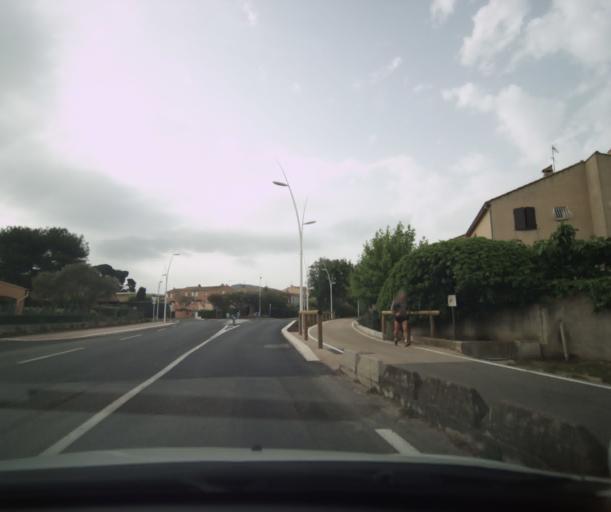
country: FR
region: Provence-Alpes-Cote d'Azur
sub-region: Departement du Var
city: Le Pradet
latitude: 43.1091
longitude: 6.0242
